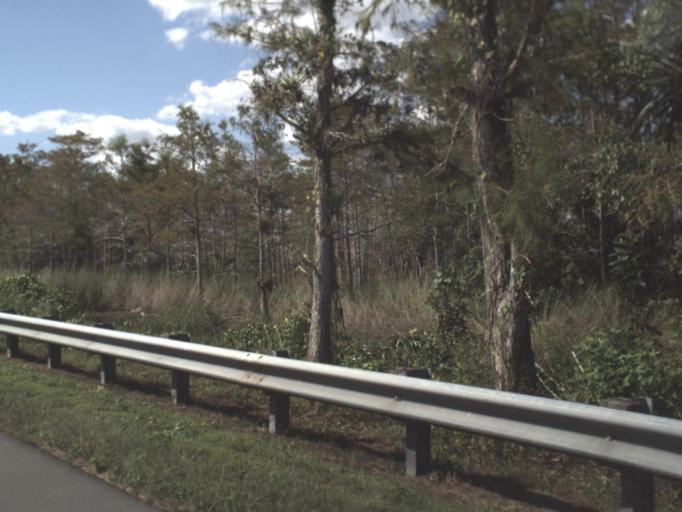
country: US
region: Florida
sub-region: Collier County
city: Immokalee
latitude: 25.8619
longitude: -81.0830
